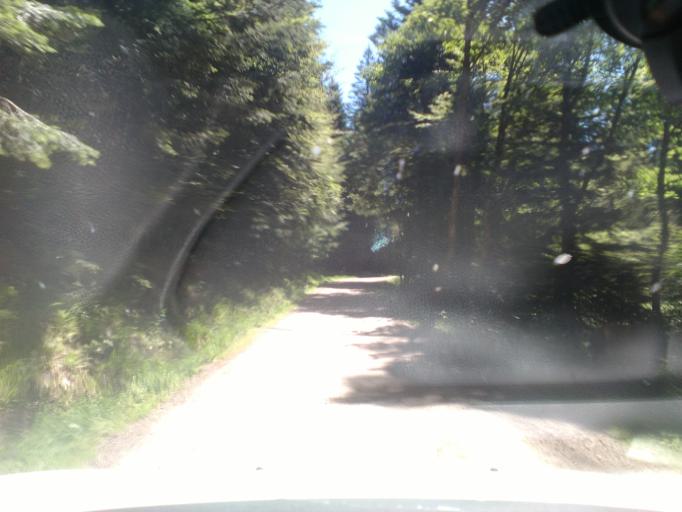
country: FR
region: Lorraine
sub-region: Departement des Vosges
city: Xonrupt-Longemer
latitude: 48.0197
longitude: 6.9733
